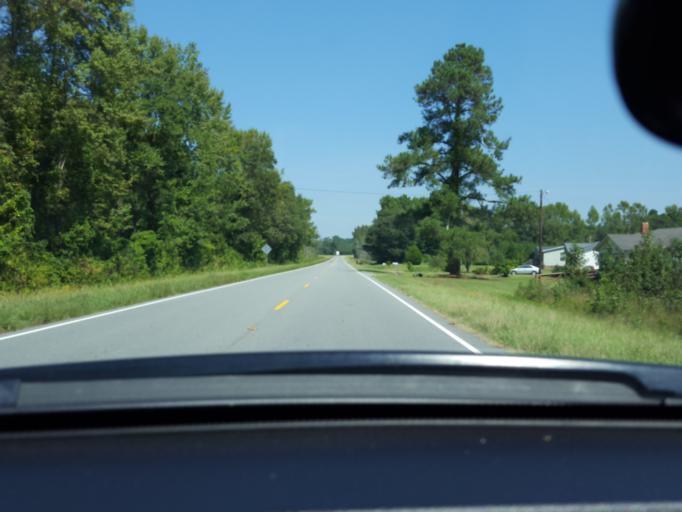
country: US
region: North Carolina
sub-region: Bladen County
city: Elizabethtown
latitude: 34.6741
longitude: -78.4901
